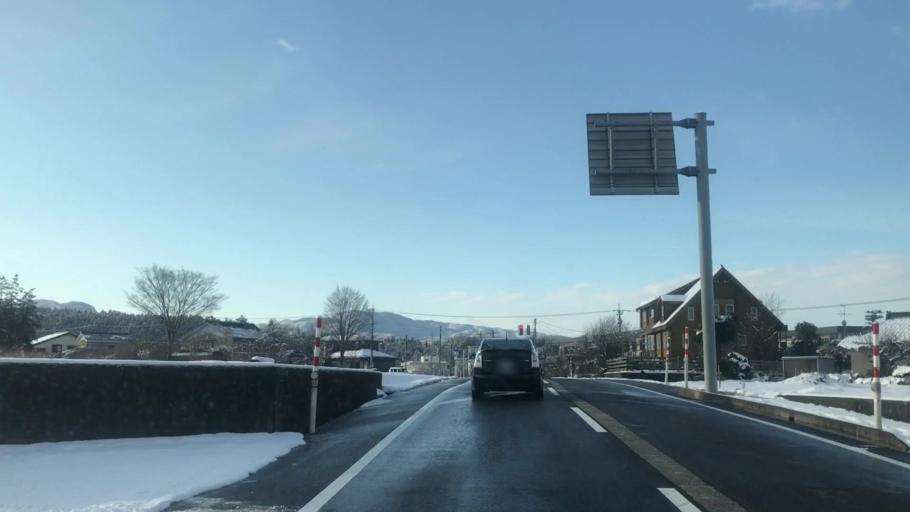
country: JP
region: Toyama
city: Toyama-shi
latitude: 36.6128
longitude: 137.2848
